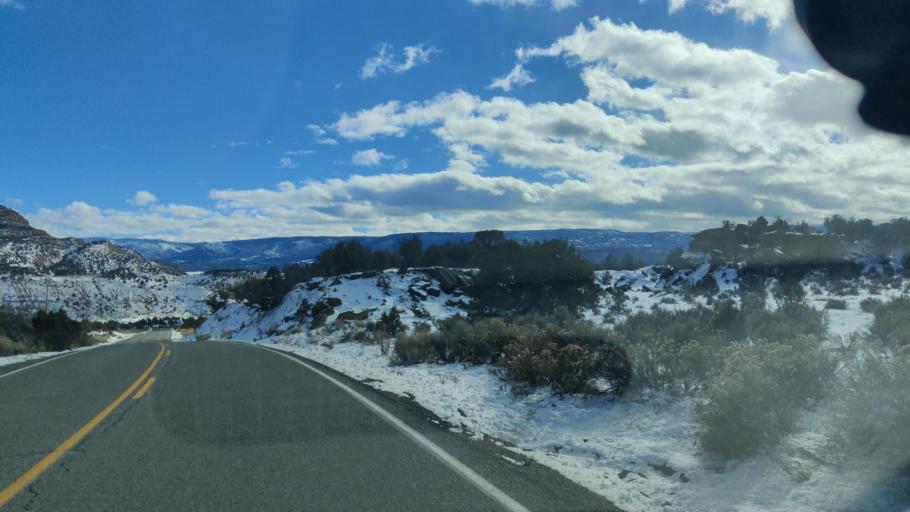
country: US
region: Colorado
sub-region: Mesa County
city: Palisade
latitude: 39.2099
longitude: -108.1470
